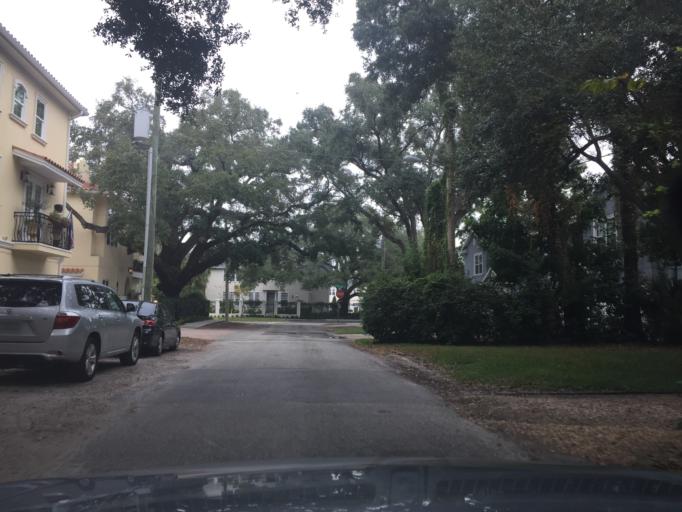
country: US
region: Florida
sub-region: Hillsborough County
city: Tampa
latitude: 27.9332
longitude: -82.4840
